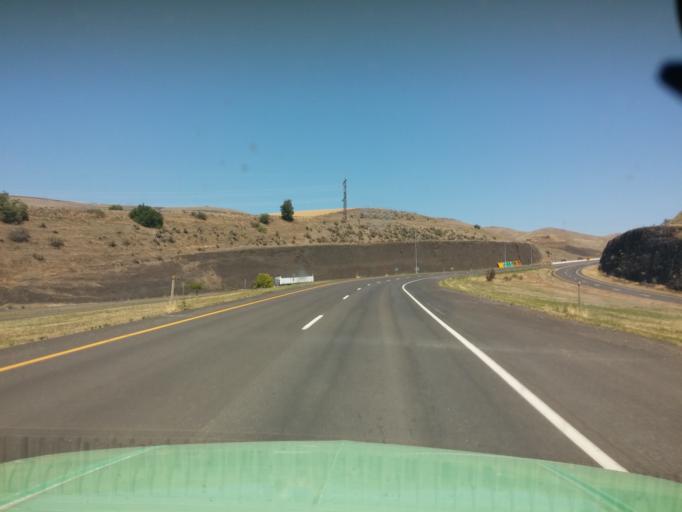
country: US
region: Idaho
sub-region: Nez Perce County
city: Lewiston
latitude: 46.4324
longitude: -116.9935
